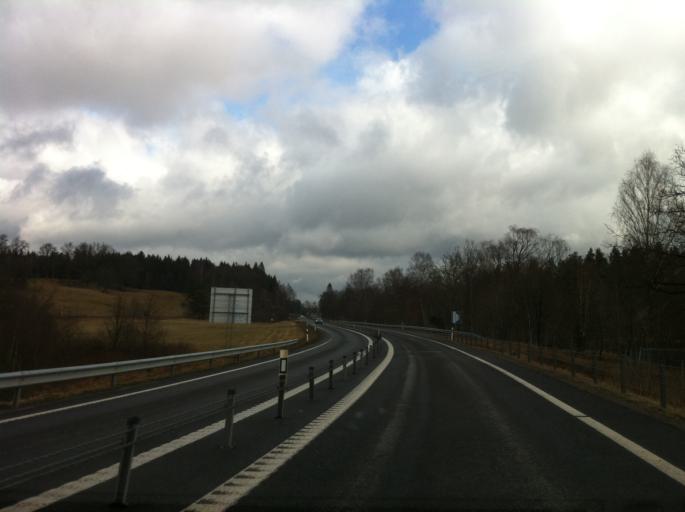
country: SE
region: Halland
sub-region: Halmstads Kommun
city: Oskarstrom
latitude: 56.8519
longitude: 13.0286
